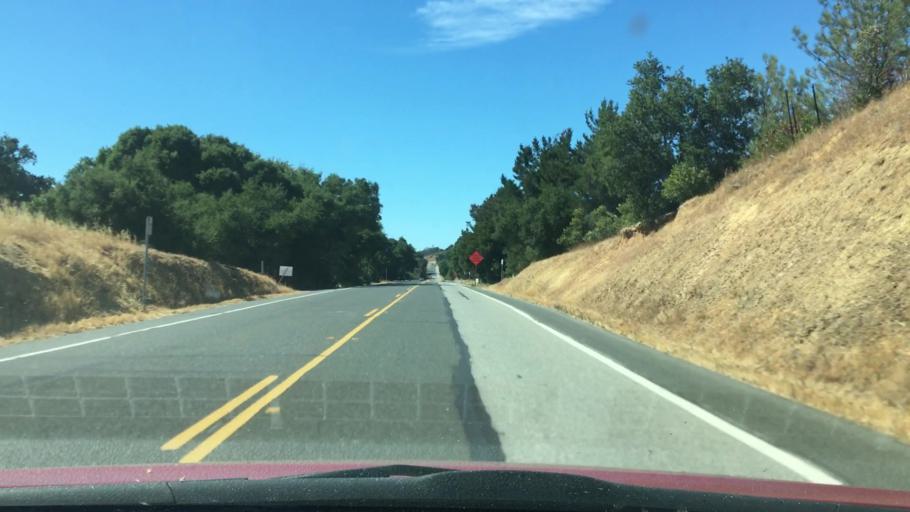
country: US
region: California
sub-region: San Mateo County
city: Emerald Lake Hills
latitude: 37.4807
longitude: -122.3128
